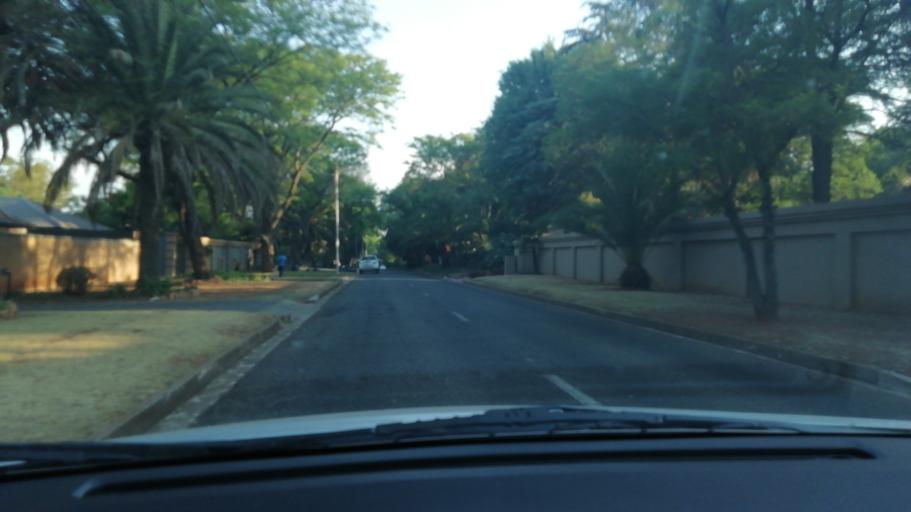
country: ZA
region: Gauteng
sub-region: Ekurhuleni Metropolitan Municipality
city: Benoni
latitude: -26.1912
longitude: 28.2883
